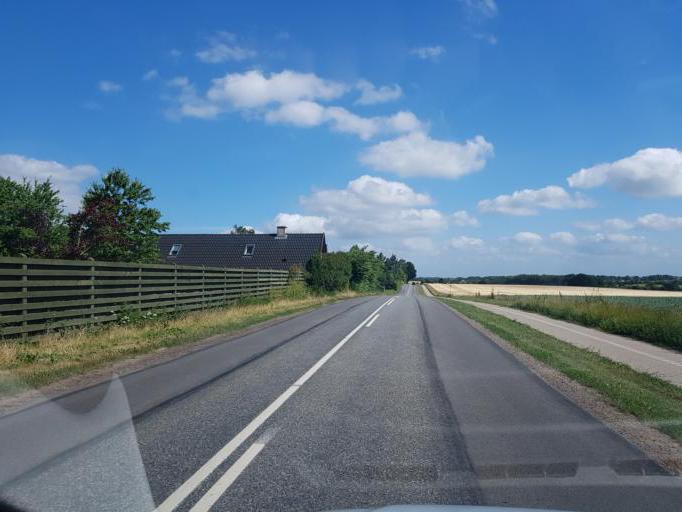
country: DK
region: Zealand
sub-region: Lejre Kommune
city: Osted
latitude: 55.5804
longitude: 11.9678
